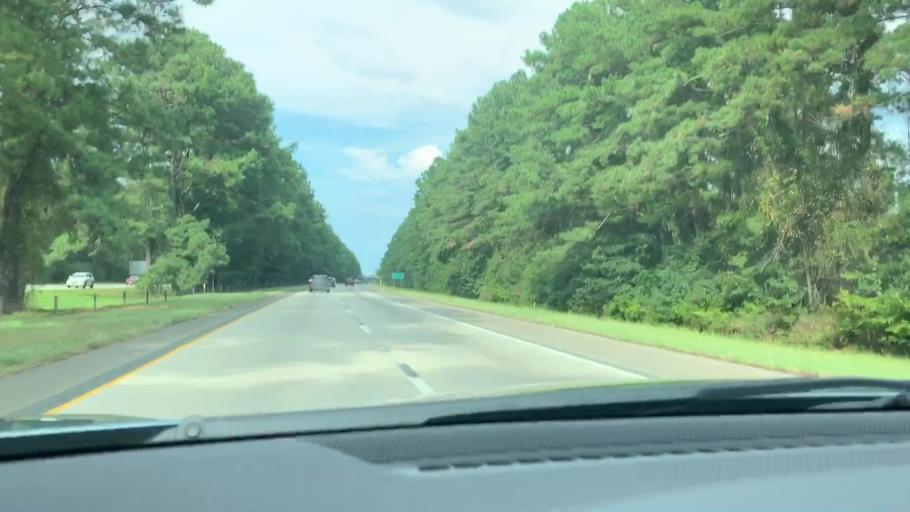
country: US
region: South Carolina
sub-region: Colleton County
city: Walterboro
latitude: 32.8904
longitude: -80.7123
